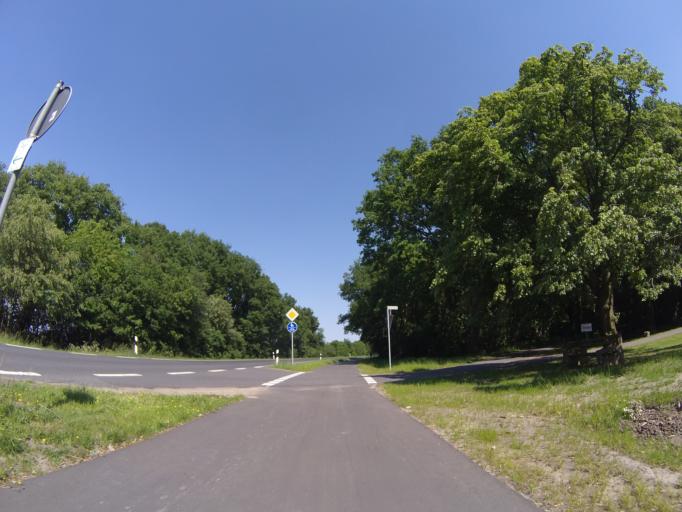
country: DE
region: Lower Saxony
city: Emlichheim
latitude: 52.6061
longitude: 6.8040
